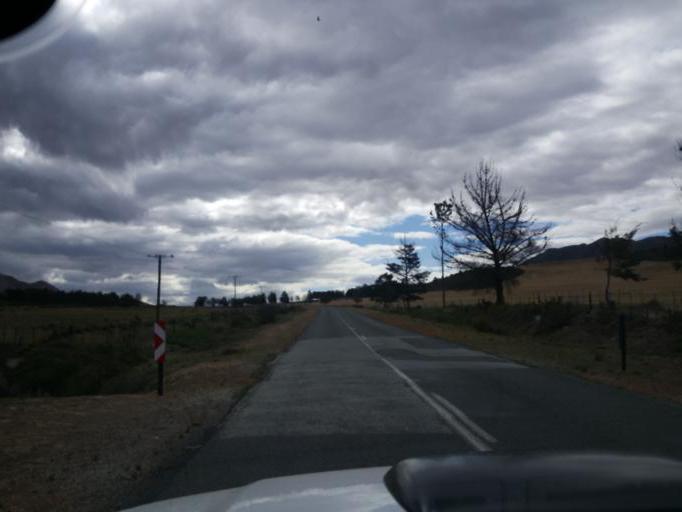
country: ZA
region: Western Cape
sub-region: Eden District Municipality
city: George
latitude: -33.8275
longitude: 22.4151
